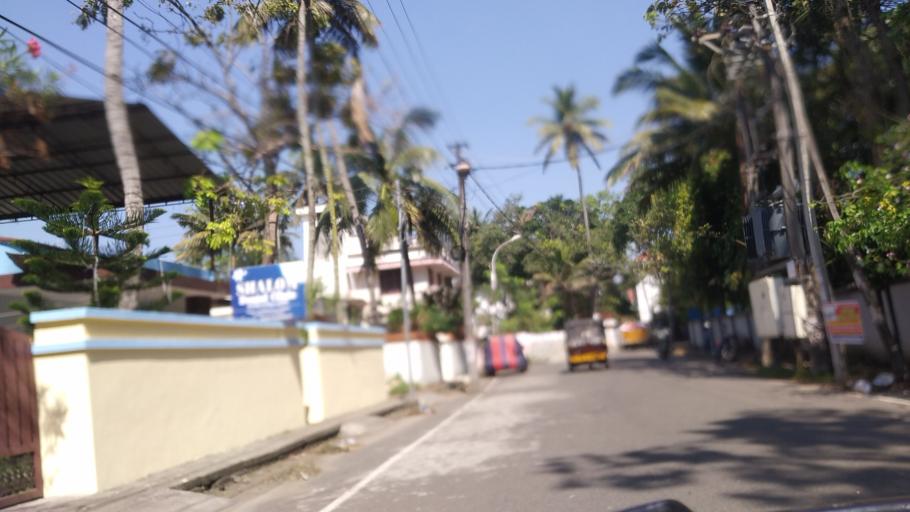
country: IN
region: Kerala
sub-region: Ernakulam
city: Cochin
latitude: 9.9368
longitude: 76.2487
